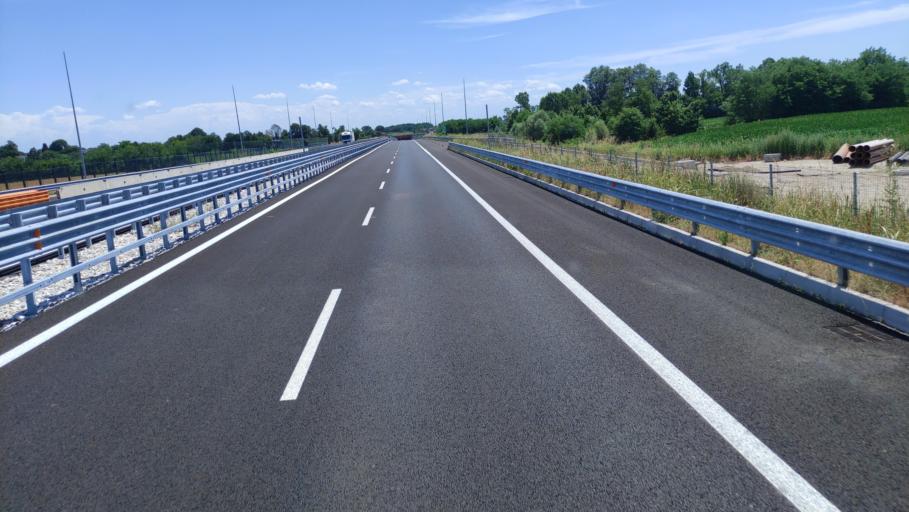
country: IT
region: Veneto
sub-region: Provincia di Treviso
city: San Vito
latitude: 45.7522
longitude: 11.8976
